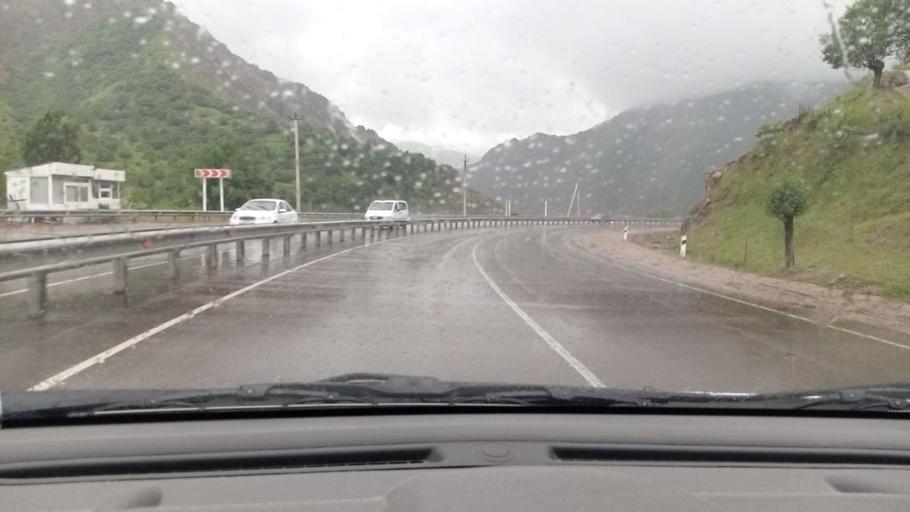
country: UZ
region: Toshkent
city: Angren
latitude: 41.1011
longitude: 70.3296
